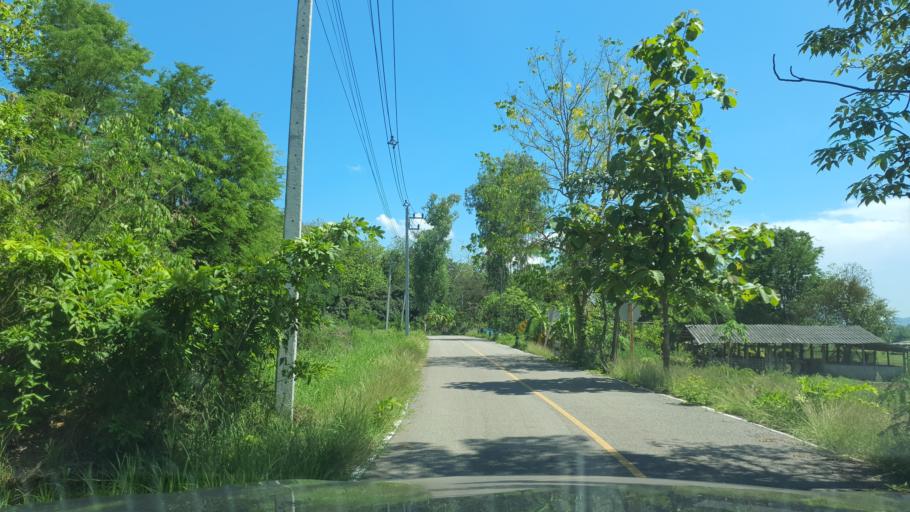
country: TH
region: Chiang Mai
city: Mae On
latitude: 18.7952
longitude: 99.2654
